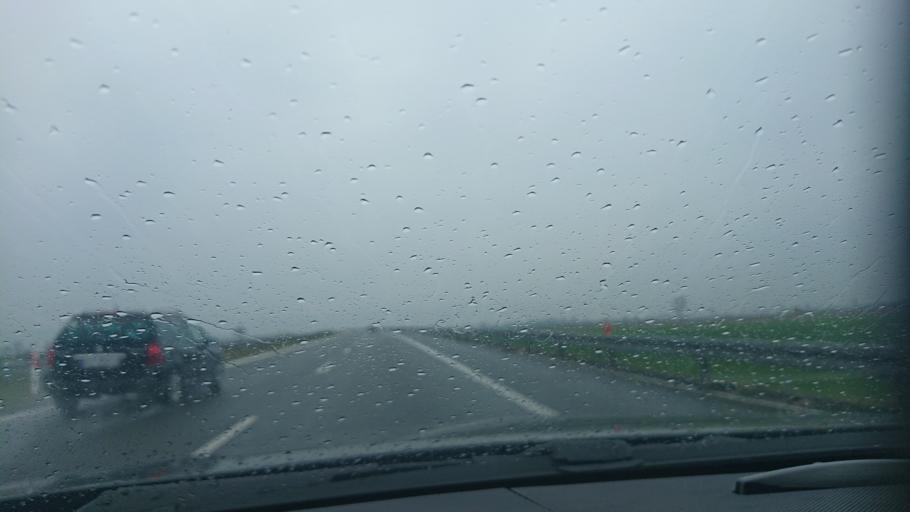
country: PL
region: Greater Poland Voivodeship
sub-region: Powiat gnieznienski
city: Gniezno
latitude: 52.5718
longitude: 17.5886
